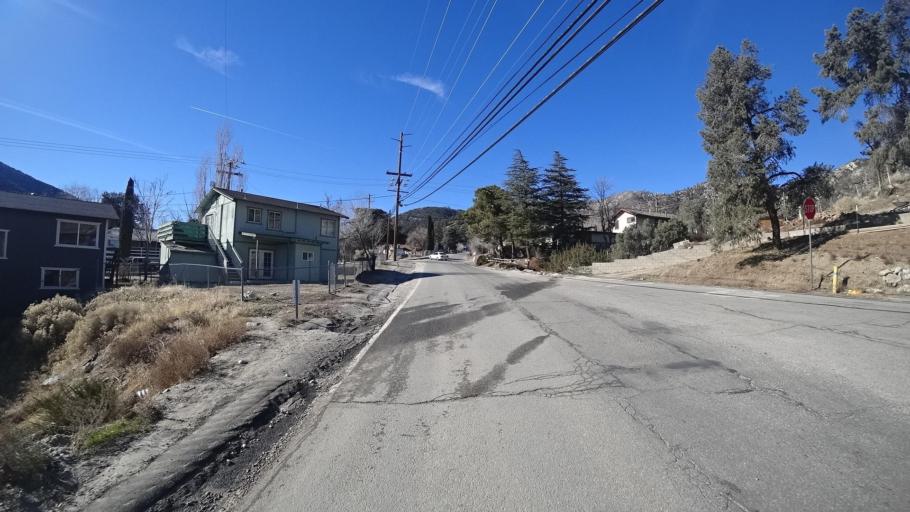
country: US
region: California
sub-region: Kern County
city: Frazier Park
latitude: 34.8229
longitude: -118.9540
